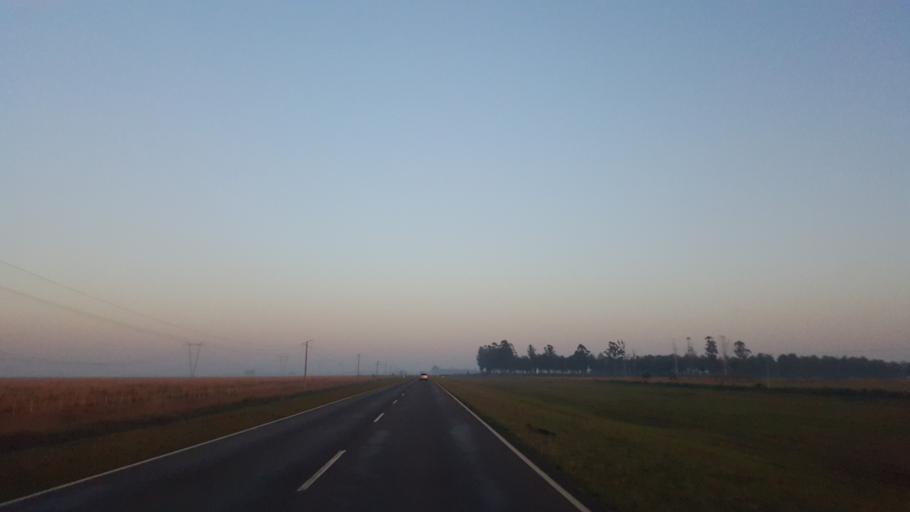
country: AR
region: Corrientes
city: Ituzaingo
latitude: -27.6016
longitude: -56.4545
